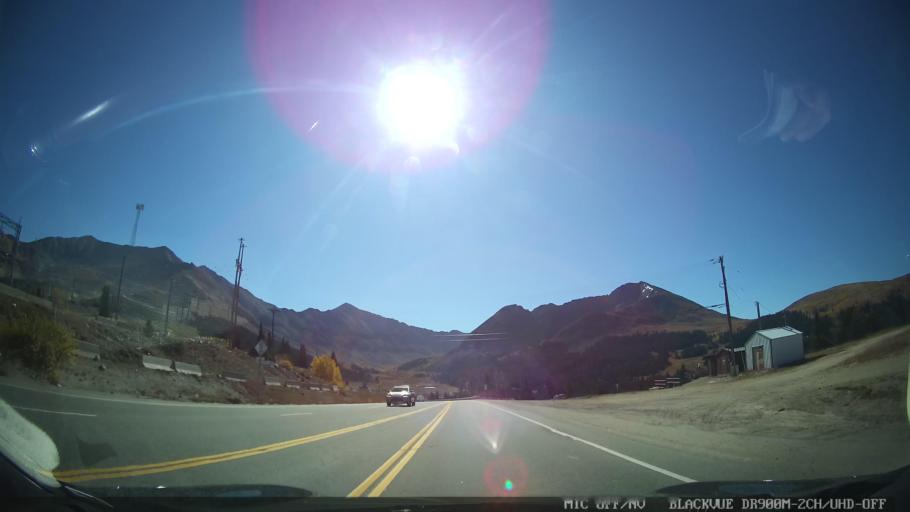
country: US
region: Colorado
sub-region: Lake County
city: Leadville
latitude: 39.3676
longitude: -106.1879
